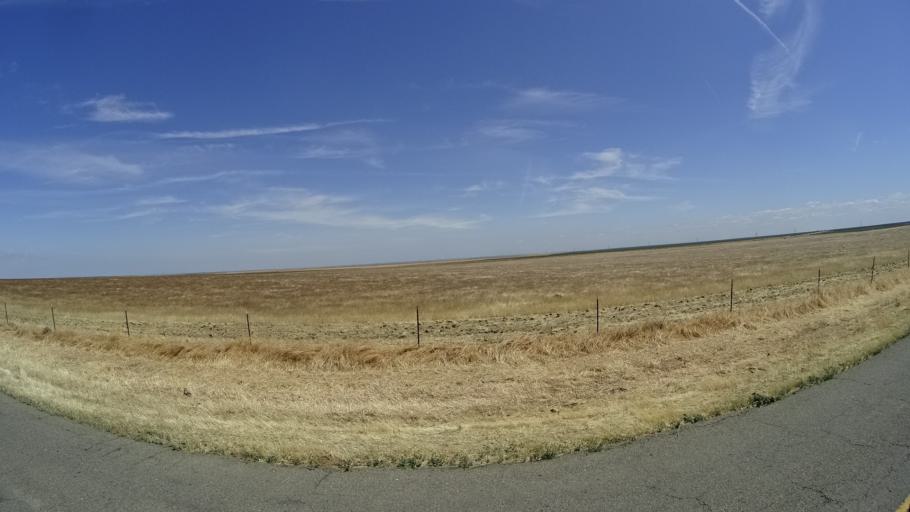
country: US
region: California
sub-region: Kings County
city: Kettleman City
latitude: 35.8007
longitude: -119.8954
